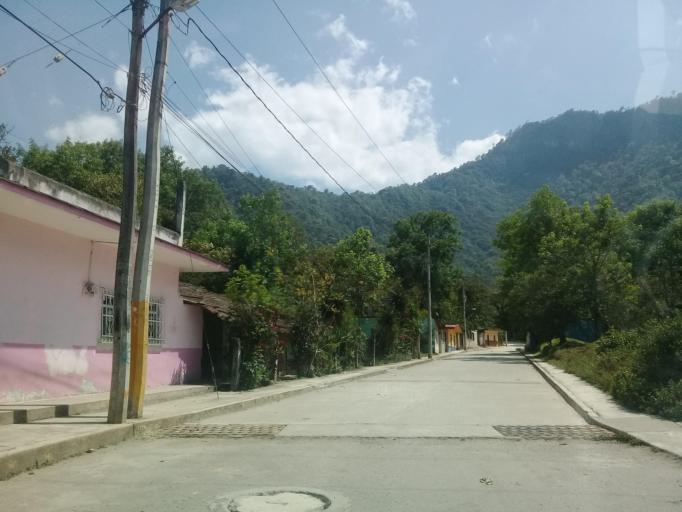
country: MX
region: Veracruz
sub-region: Tlilapan
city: Tonalixco
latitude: 18.8056
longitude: -97.0697
